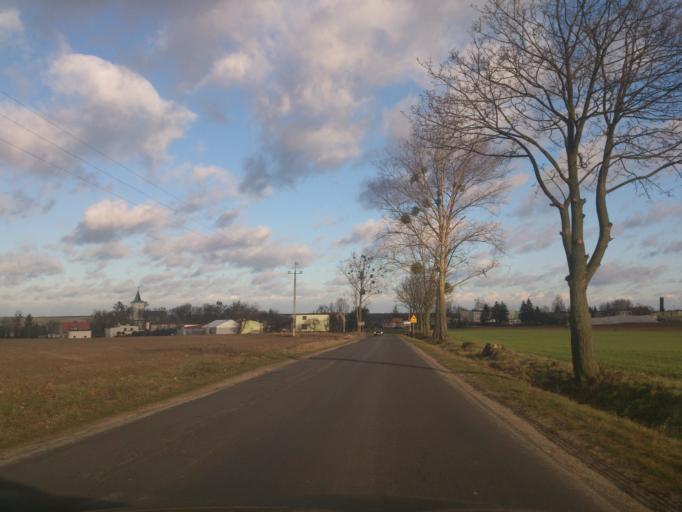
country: PL
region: Kujawsko-Pomorskie
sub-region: Powiat golubsko-dobrzynski
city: Ciechocin
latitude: 53.0542
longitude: 18.9189
